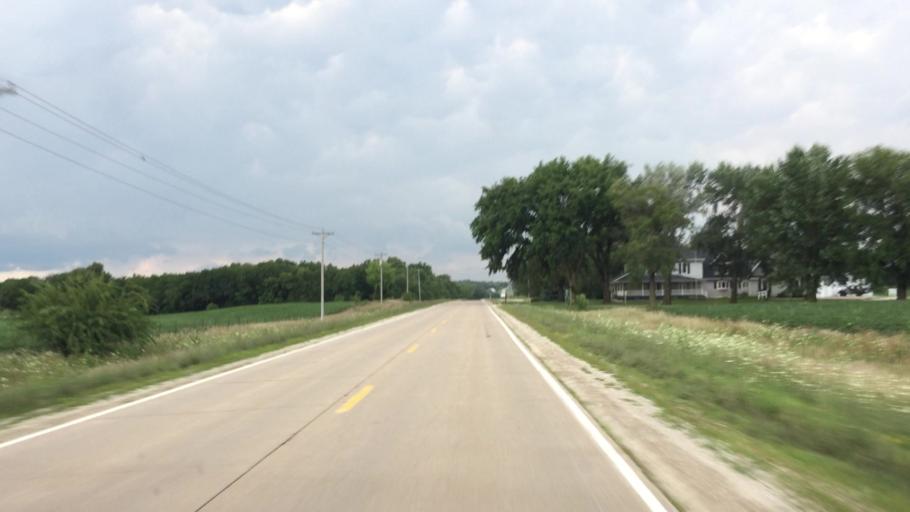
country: US
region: Iowa
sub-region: Lee County
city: Fort Madison
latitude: 40.7081
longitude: -91.3299
